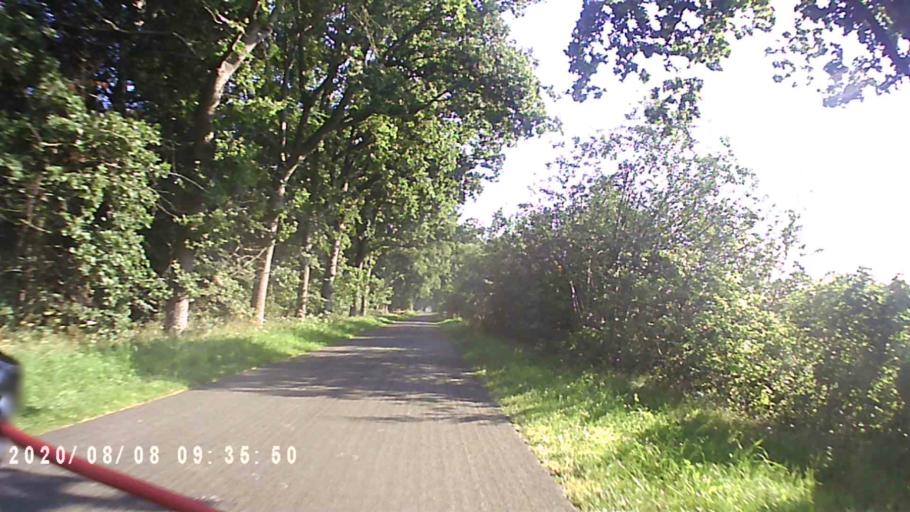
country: NL
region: Groningen
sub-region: Gemeente Leek
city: Leek
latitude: 53.0479
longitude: 6.3834
